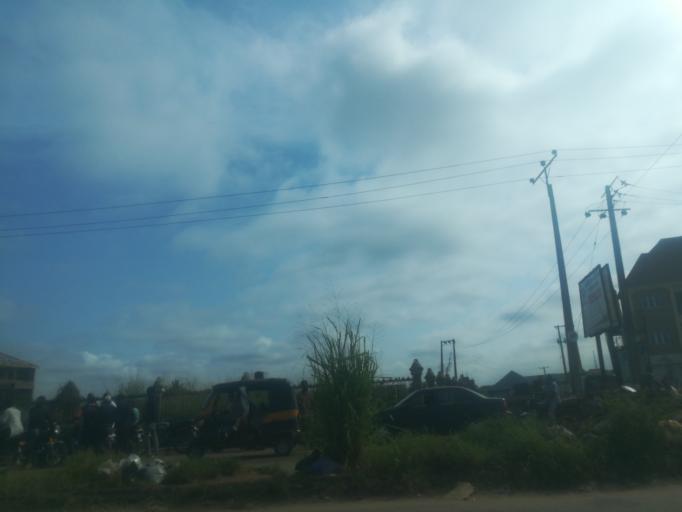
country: NG
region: Oyo
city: Ibadan
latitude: 7.3379
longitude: 3.8546
